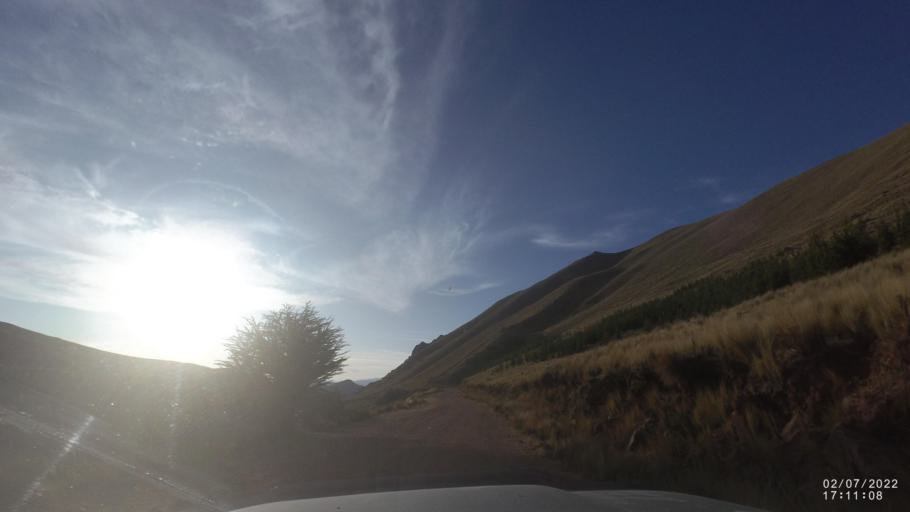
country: BO
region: Cochabamba
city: Irpa Irpa
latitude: -17.8922
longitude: -66.5636
